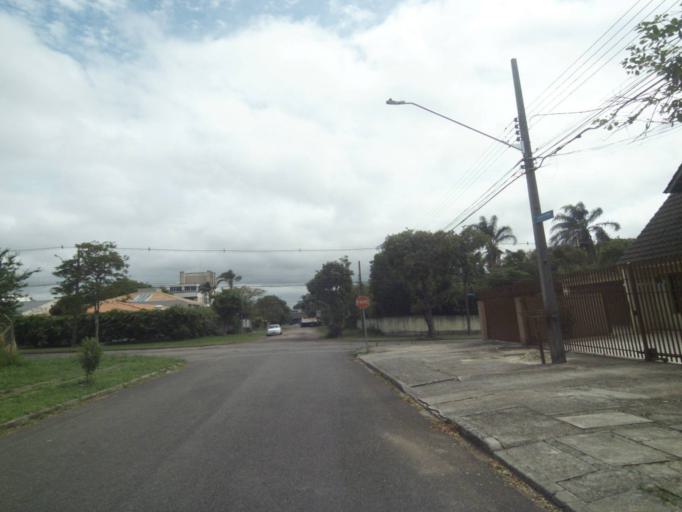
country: BR
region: Parana
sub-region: Pinhais
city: Pinhais
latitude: -25.4311
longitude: -49.2266
